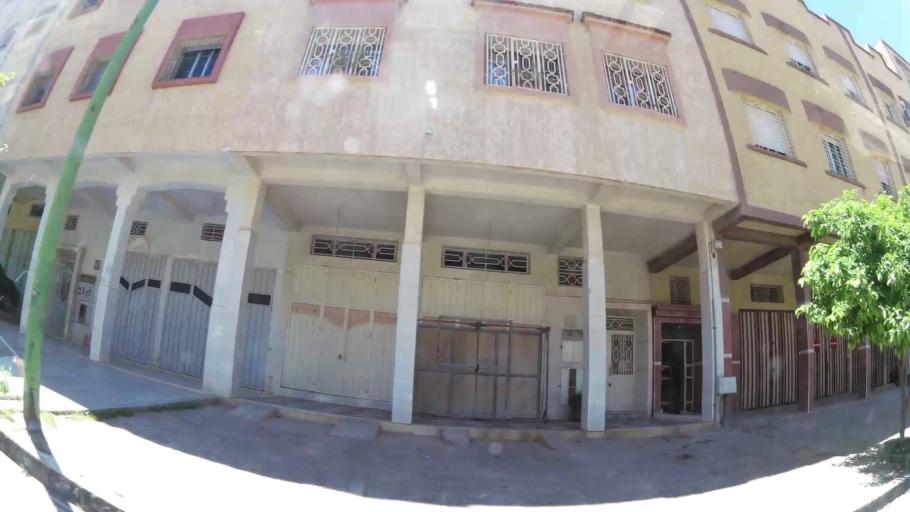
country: MA
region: Meknes-Tafilalet
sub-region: Meknes
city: Meknes
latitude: 33.8511
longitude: -5.5575
